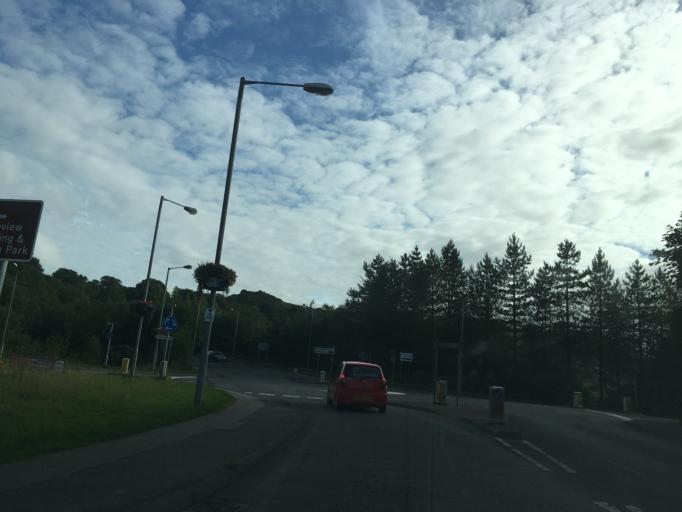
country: GB
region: Scotland
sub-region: Argyll and Bute
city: Oban
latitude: 56.4017
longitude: -5.4728
